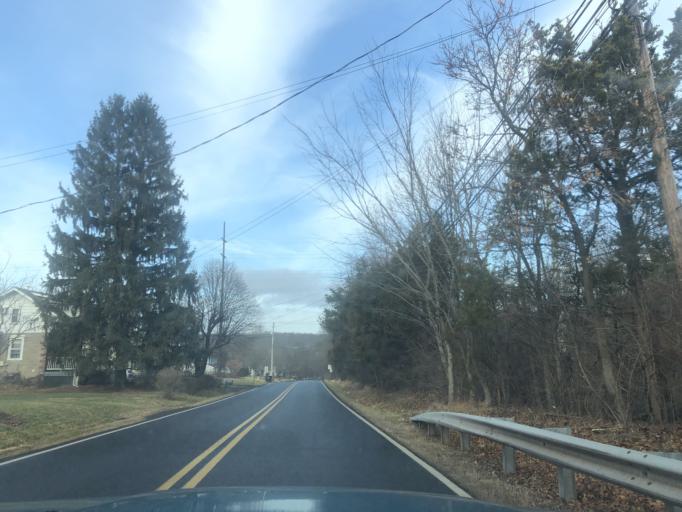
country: US
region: Pennsylvania
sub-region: Bucks County
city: Perkasie
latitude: 40.3790
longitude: -75.3087
